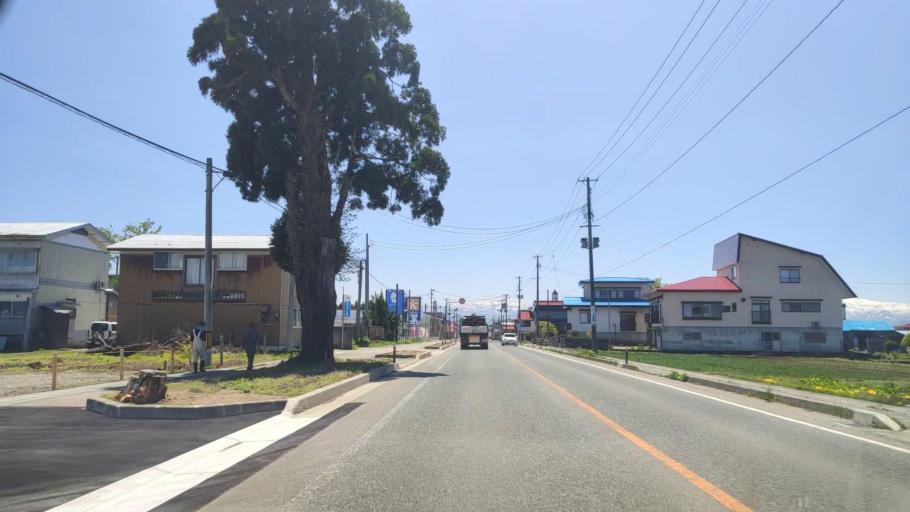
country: JP
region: Yamagata
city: Shinjo
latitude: 38.8142
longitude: 140.3244
